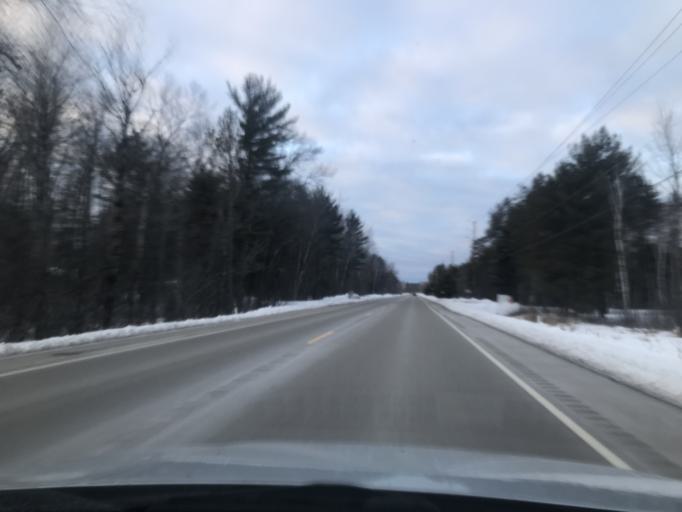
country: US
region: Wisconsin
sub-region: Marinette County
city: Marinette
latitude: 45.1325
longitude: -87.6880
